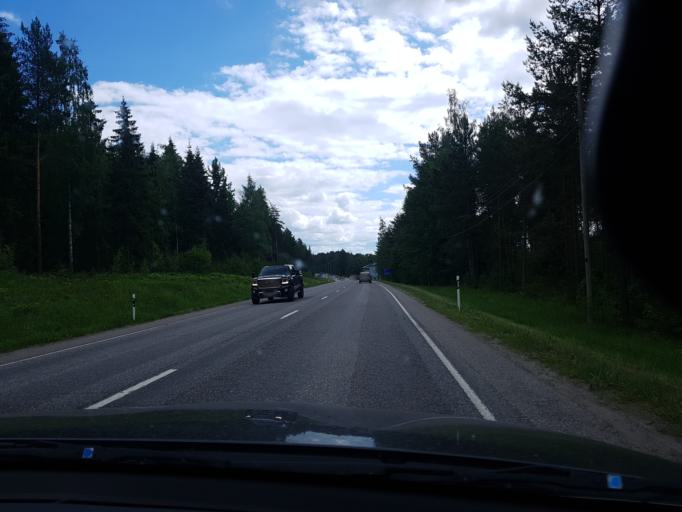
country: FI
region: Pirkanmaa
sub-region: Tampere
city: Paelkaene
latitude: 61.3043
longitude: 24.2991
